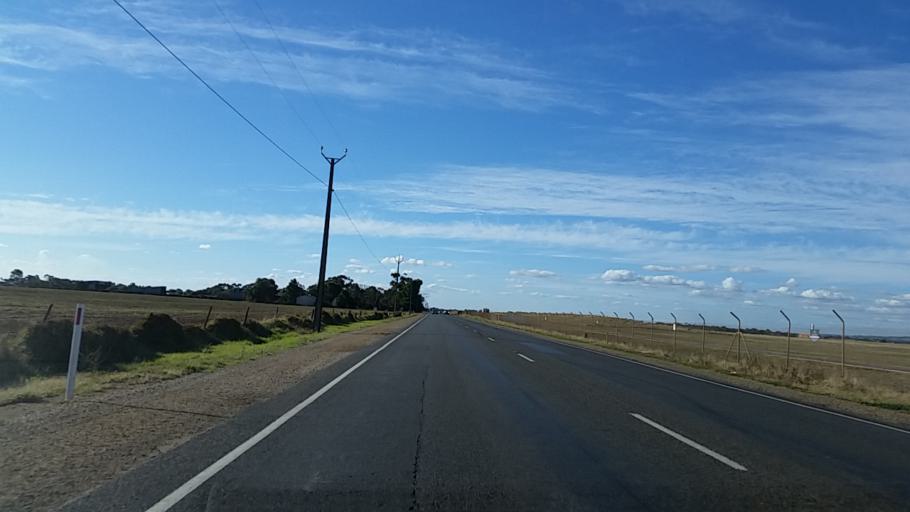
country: AU
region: South Australia
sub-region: Playford
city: Virginia
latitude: -34.7088
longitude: 138.6056
